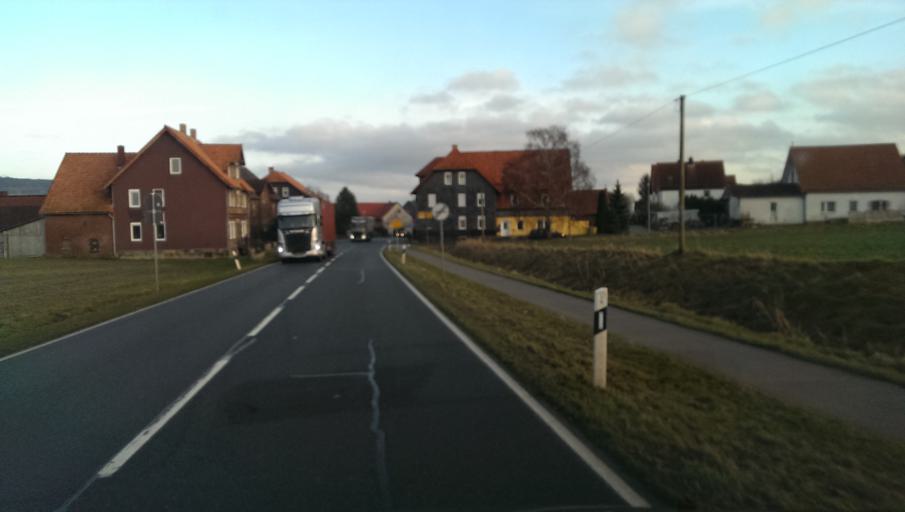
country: DE
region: Lower Saxony
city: Eimen
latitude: 51.8871
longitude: 9.7464
